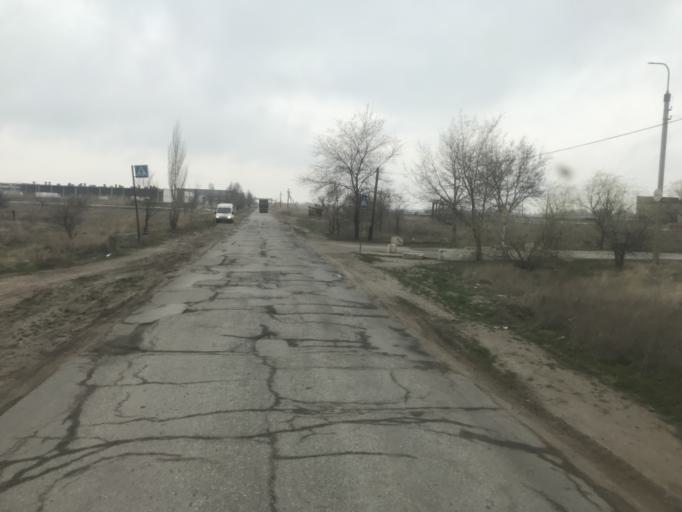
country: RU
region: Volgograd
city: Svetlyy Yar
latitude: 48.5225
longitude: 44.6205
